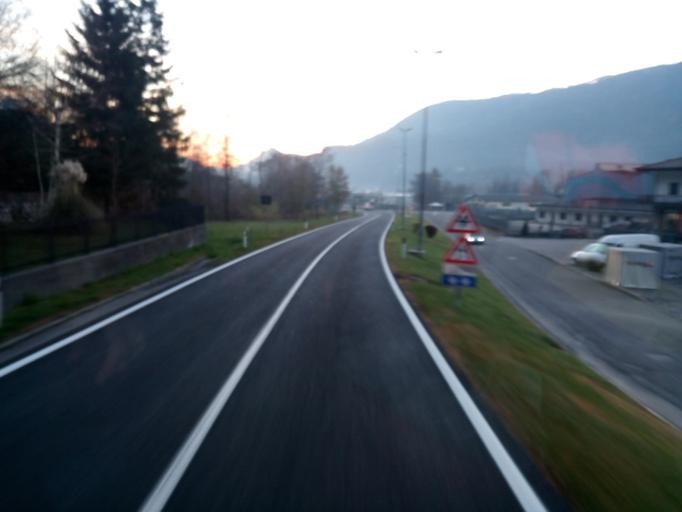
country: IT
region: Friuli Venezia Giulia
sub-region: Provincia di Udine
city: Villa Santina
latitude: 46.4145
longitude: 12.9317
